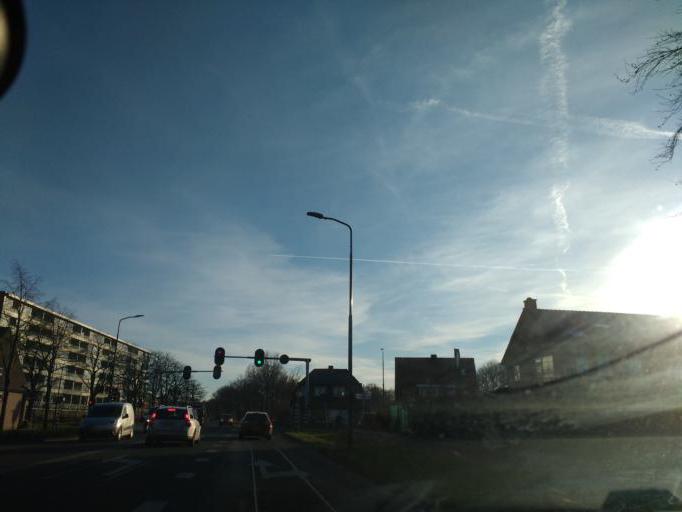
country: NL
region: Utrecht
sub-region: Gemeente Veenendaal
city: Veenendaal
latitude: 52.0196
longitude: 5.5374
